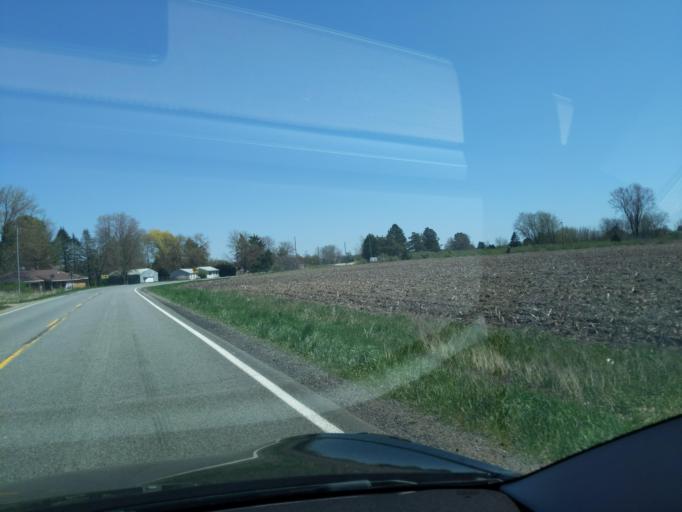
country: US
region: Michigan
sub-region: Ingham County
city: Mason
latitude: 42.5670
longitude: -84.4564
